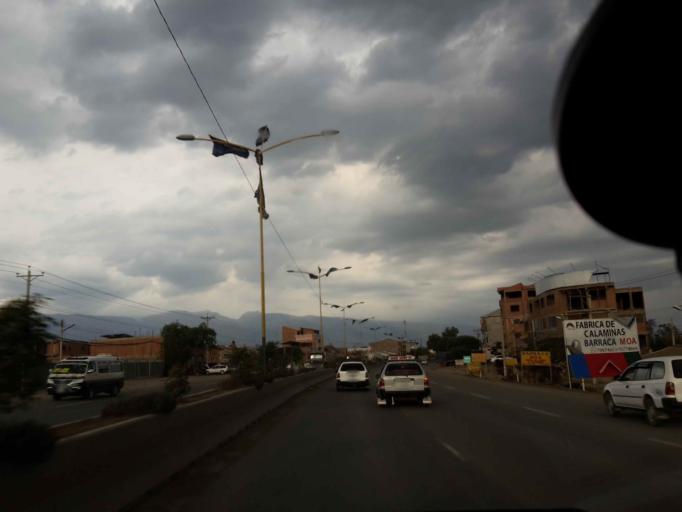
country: BO
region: Cochabamba
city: Sipe Sipe
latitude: -17.3968
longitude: -66.3239
